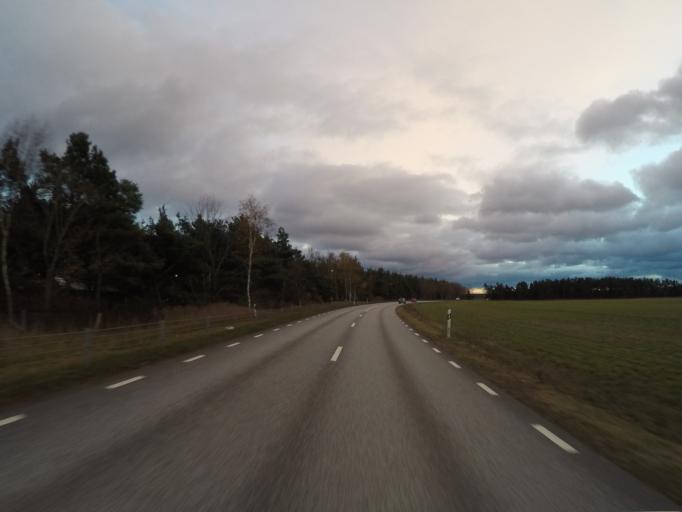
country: SE
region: Skane
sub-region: Kristianstads Kommun
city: Norra Asum
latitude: 55.9346
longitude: 14.0747
